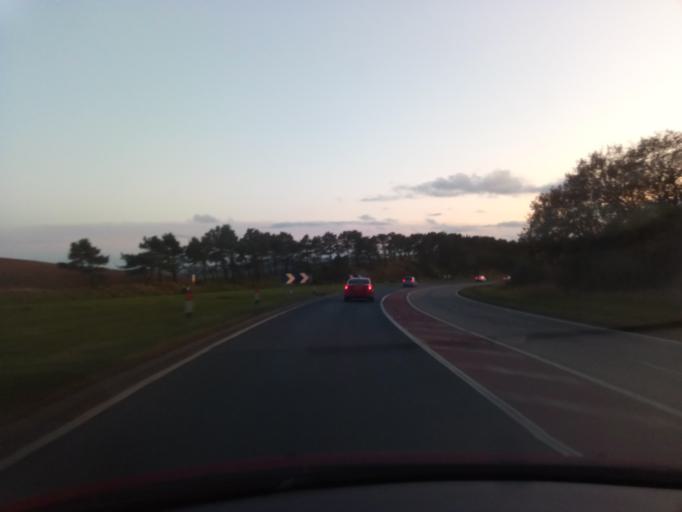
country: GB
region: Scotland
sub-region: East Lothian
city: Pencaitland
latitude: 55.8048
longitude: -2.8349
